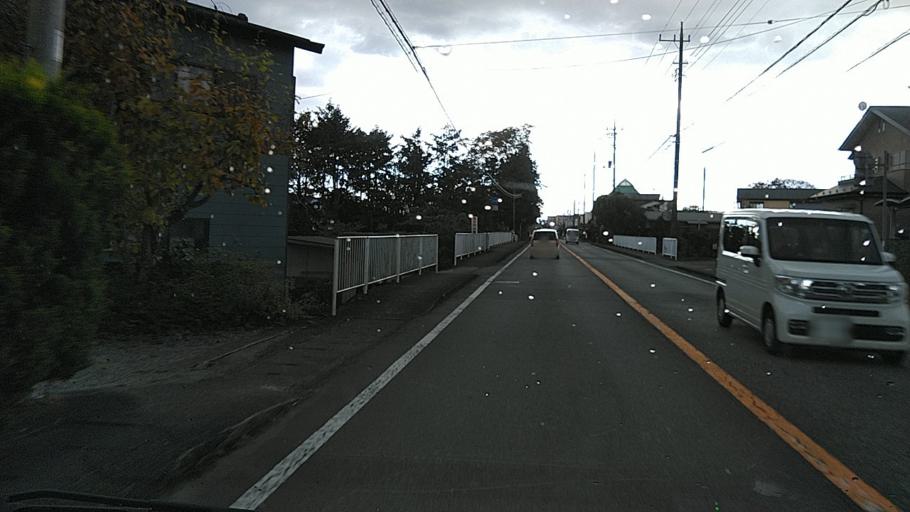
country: JP
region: Shizuoka
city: Gotemba
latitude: 35.3234
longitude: 138.9433
